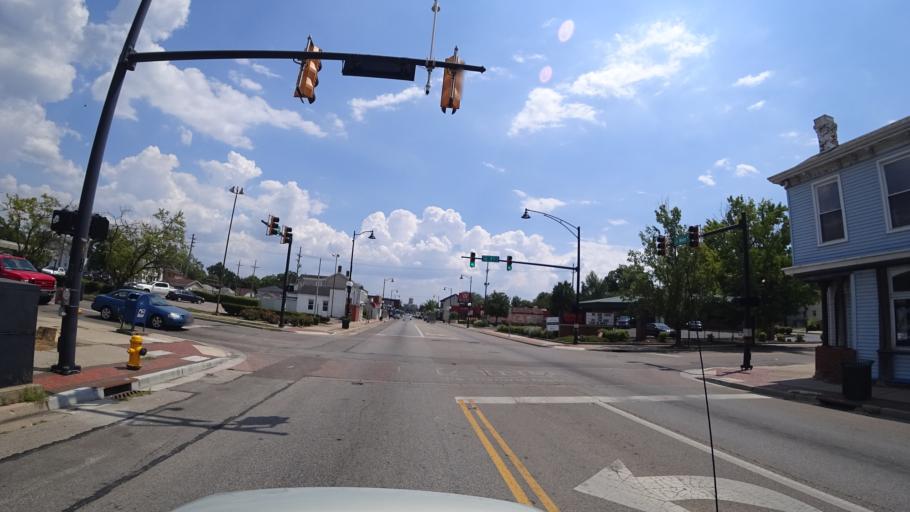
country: US
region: Ohio
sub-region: Butler County
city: Hamilton
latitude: 39.4057
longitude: -84.5718
